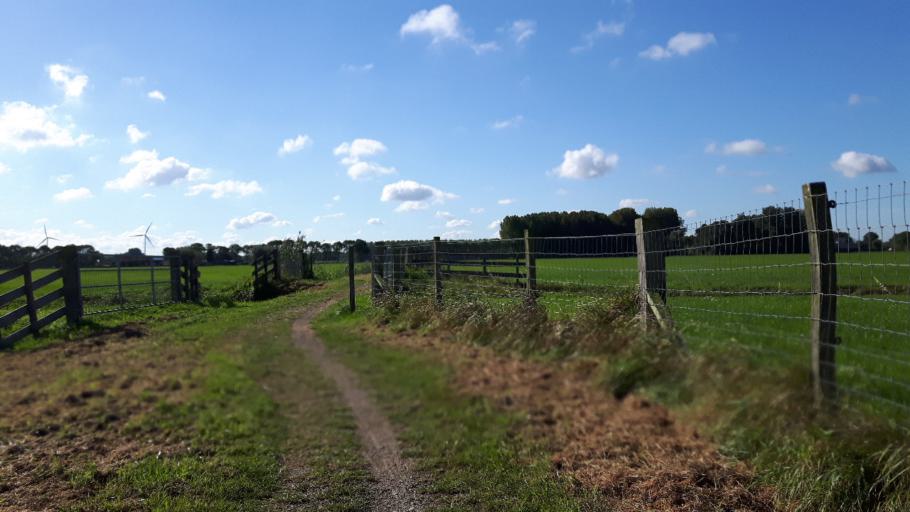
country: NL
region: Gelderland
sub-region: Gemeente Culemborg
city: Culemborg
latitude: 51.9553
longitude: 5.1877
